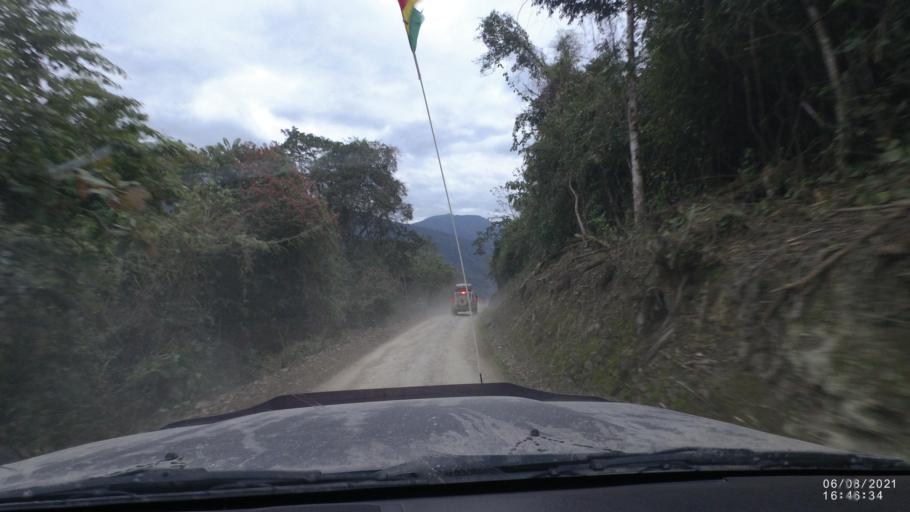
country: BO
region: La Paz
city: Quime
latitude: -16.5055
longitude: -66.7606
